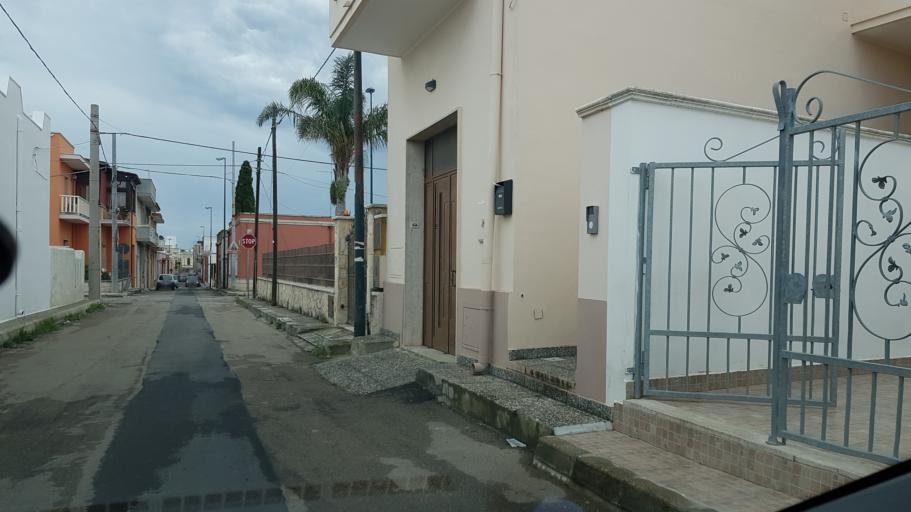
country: IT
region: Apulia
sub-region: Provincia di Brindisi
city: Torchiarolo
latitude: 40.4810
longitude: 18.0509
